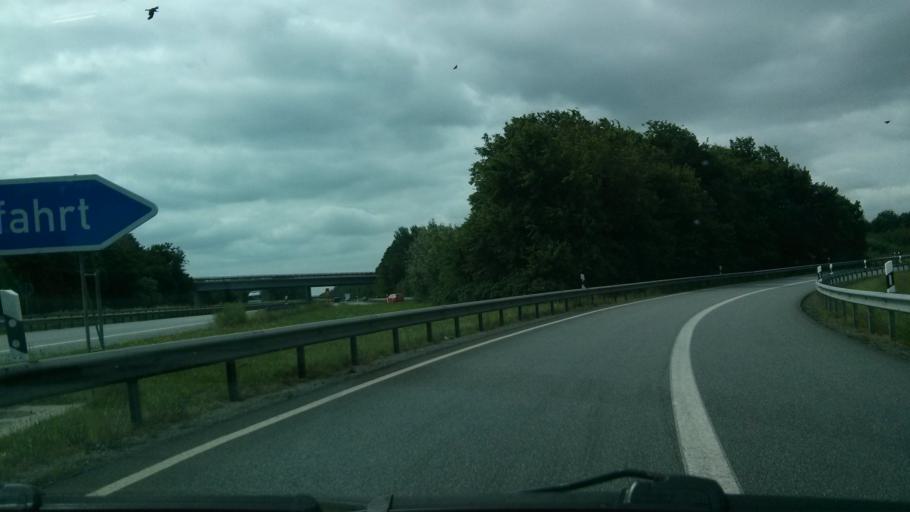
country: DE
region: Lower Saxony
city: Driftsethe
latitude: 53.4440
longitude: 8.5839
